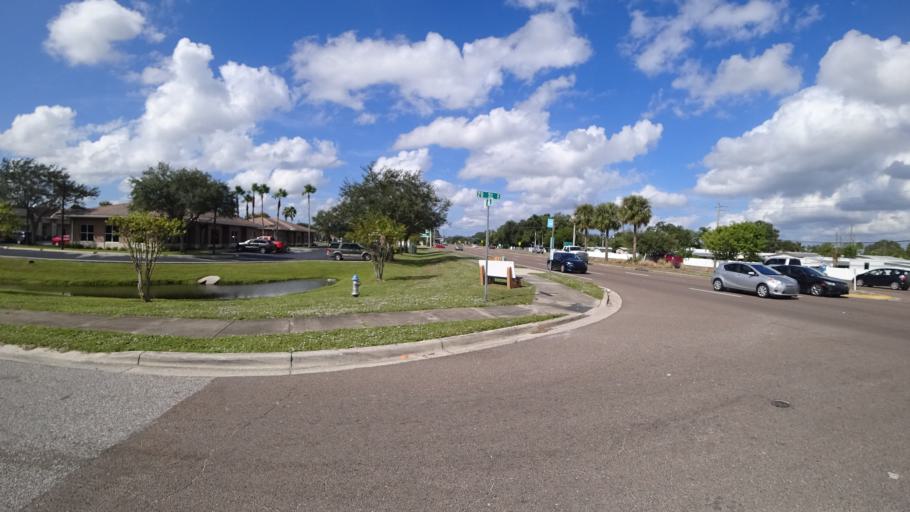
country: US
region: Florida
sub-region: Manatee County
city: Ellenton
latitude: 27.4958
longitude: -82.5276
